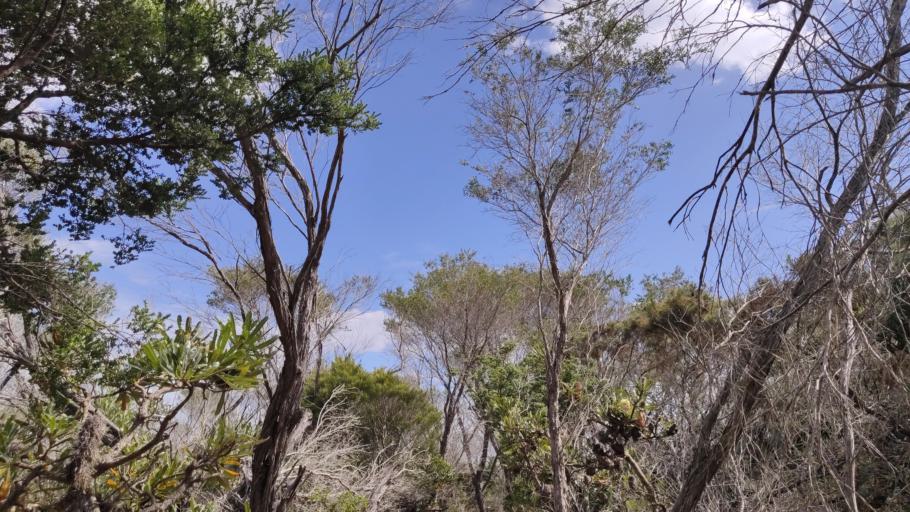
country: AU
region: New South Wales
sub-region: Port Macquarie-Hastings
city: North Haven
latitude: -31.6452
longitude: 152.8407
